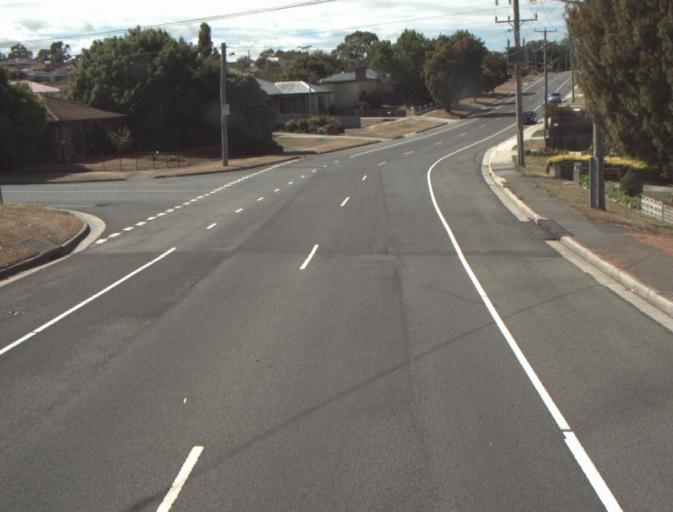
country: AU
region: Tasmania
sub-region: Launceston
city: Mayfield
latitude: -41.3874
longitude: 147.1165
